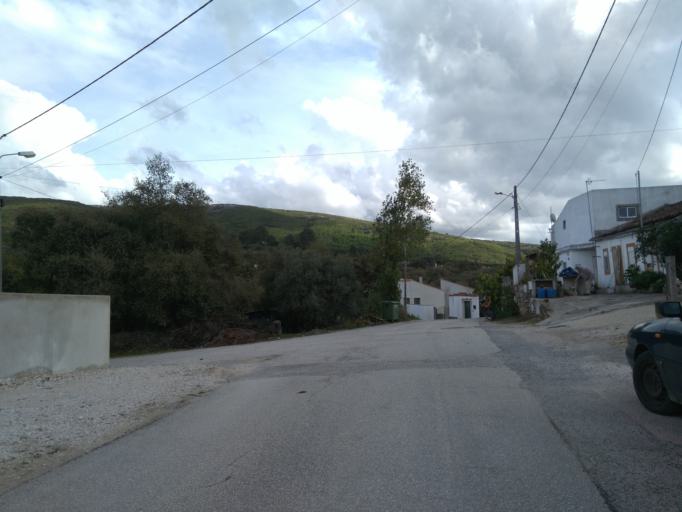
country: PT
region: Leiria
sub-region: Porto de Mos
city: Porto de Mos
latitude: 39.5970
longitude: -8.8085
